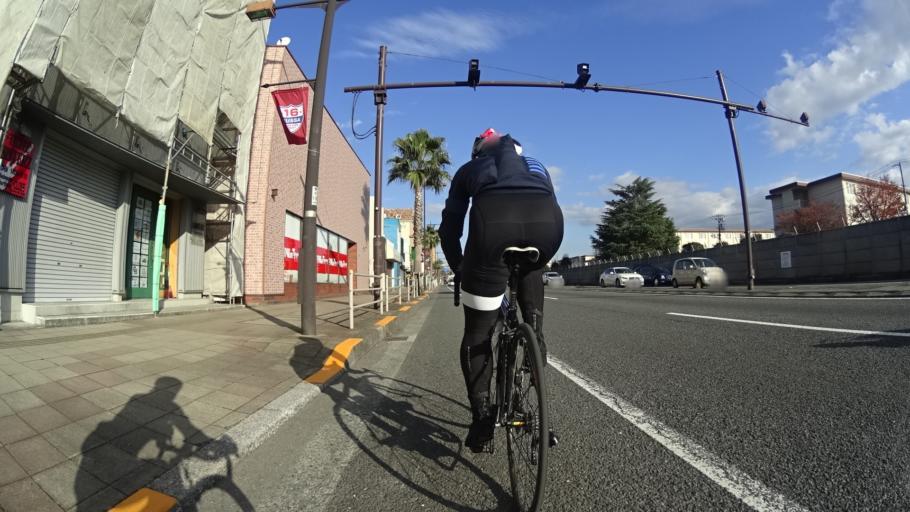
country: JP
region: Tokyo
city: Fussa
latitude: 35.7435
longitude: 139.3377
